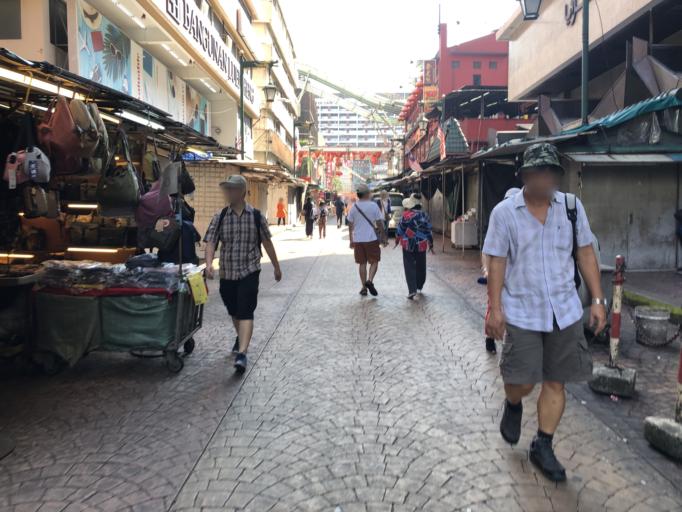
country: MY
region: Kuala Lumpur
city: Kuala Lumpur
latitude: 3.1443
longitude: 101.6969
